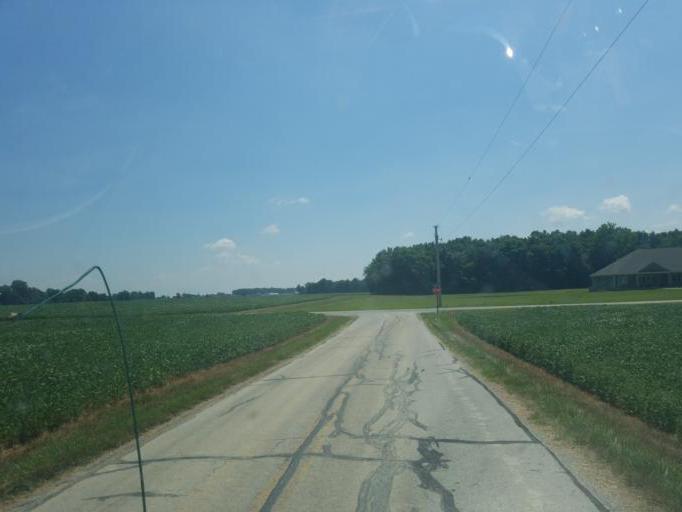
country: US
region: Ohio
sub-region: Shelby County
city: Botkins
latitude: 40.4826
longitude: -84.2310
